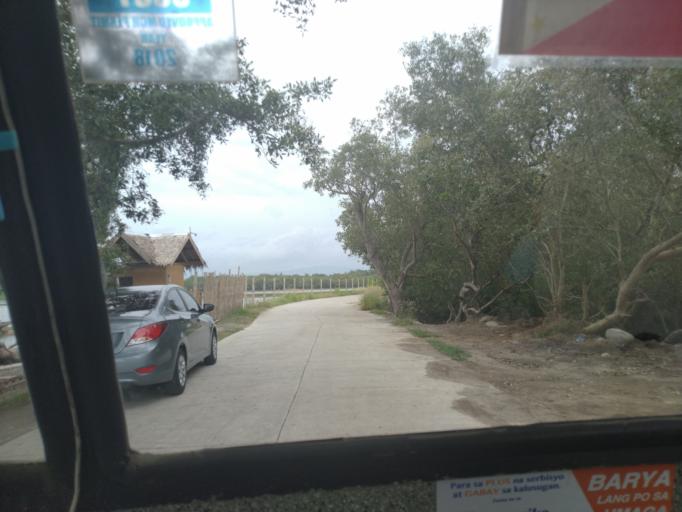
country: PH
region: Central Visayas
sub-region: Province of Negros Oriental
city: Tanjay
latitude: 9.5426
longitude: 123.1538
